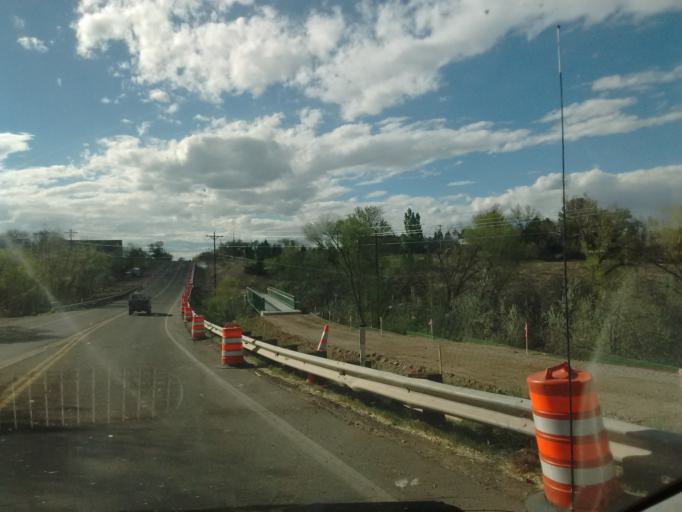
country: US
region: Colorado
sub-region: Mesa County
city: Redlands
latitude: 39.0698
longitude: -108.6158
